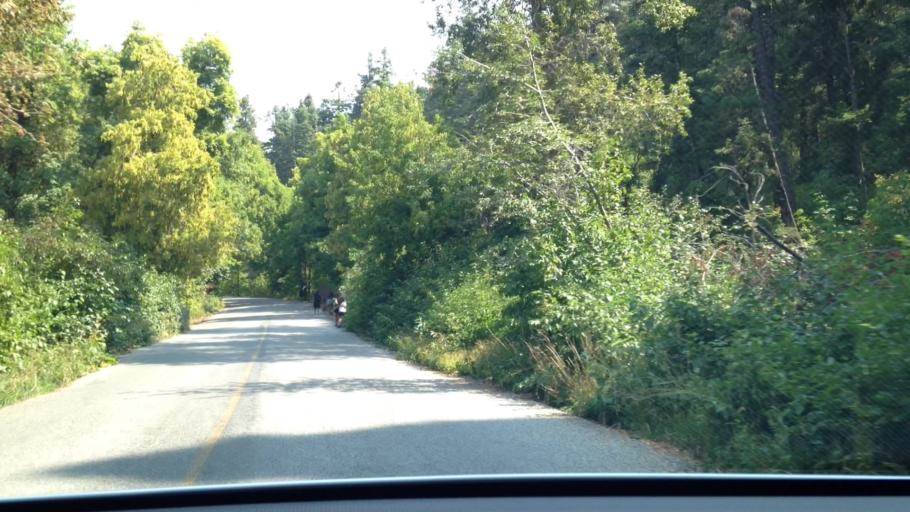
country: US
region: Utah
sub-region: Salt Lake County
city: Mount Olympus
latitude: 40.7008
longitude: -111.7007
